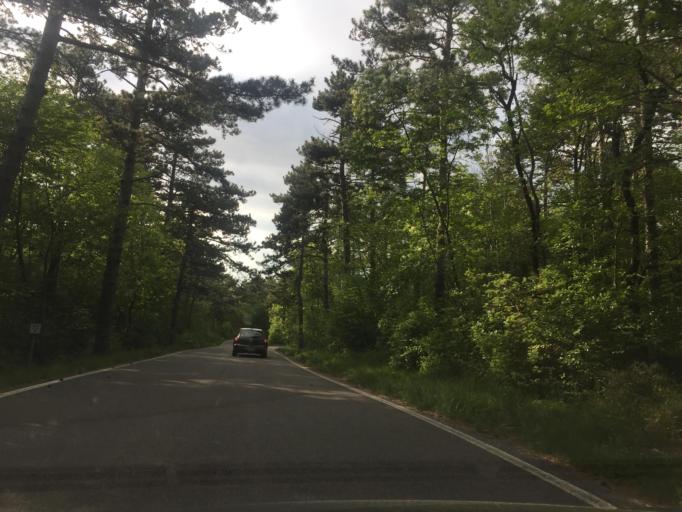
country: IT
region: Friuli Venezia Giulia
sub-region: Provincia di Trieste
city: Dolina
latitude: 45.6314
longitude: 13.8769
